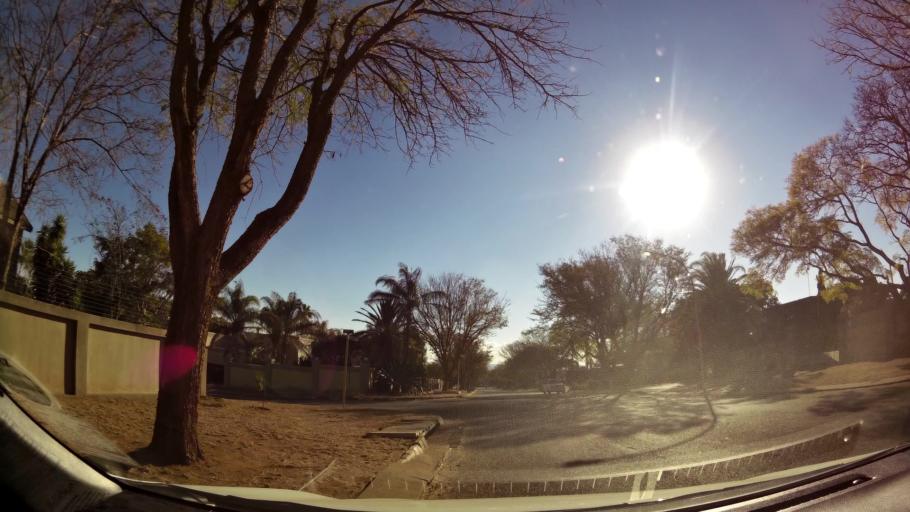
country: ZA
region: Limpopo
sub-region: Capricorn District Municipality
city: Polokwane
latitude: -23.8903
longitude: 29.4829
